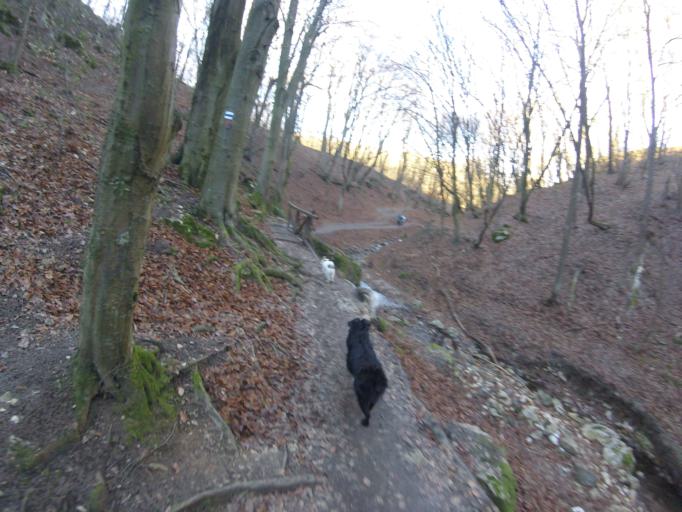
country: HU
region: Pest
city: Pilisszentkereszt
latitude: 47.6857
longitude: 18.9102
